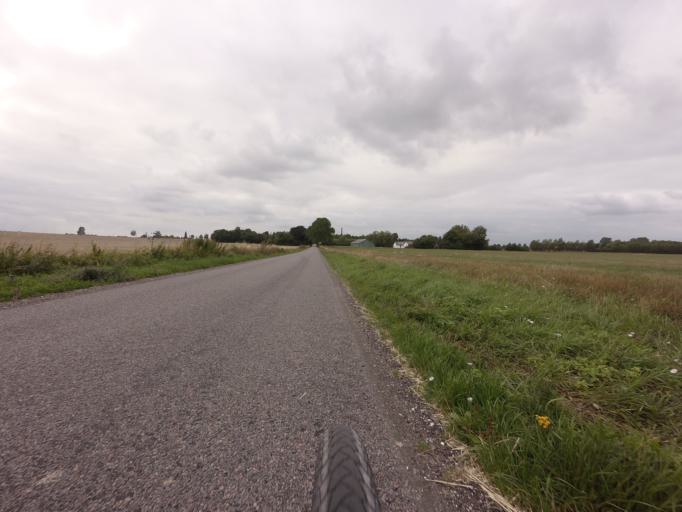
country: DK
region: Zealand
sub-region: Stevns Kommune
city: Store Heddinge
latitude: 55.3401
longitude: 12.4201
